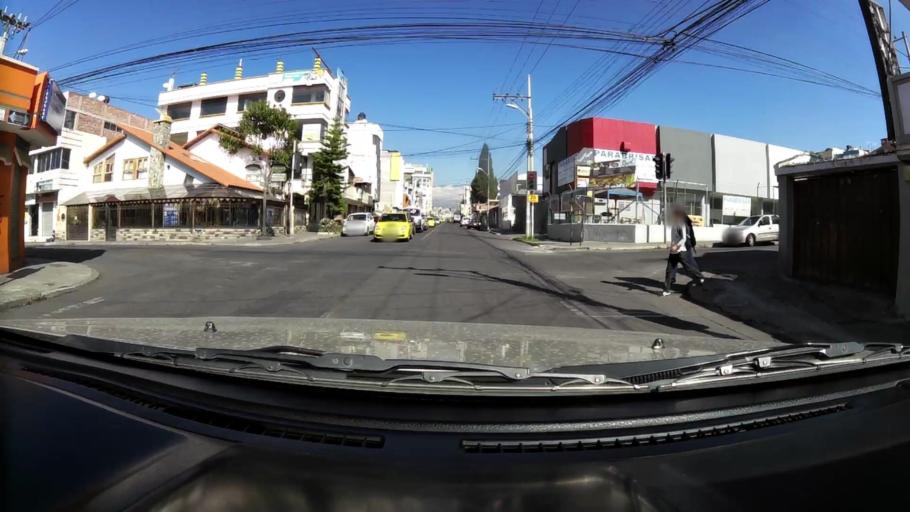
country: EC
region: Chimborazo
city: Riobamba
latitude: -1.6640
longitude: -78.6578
